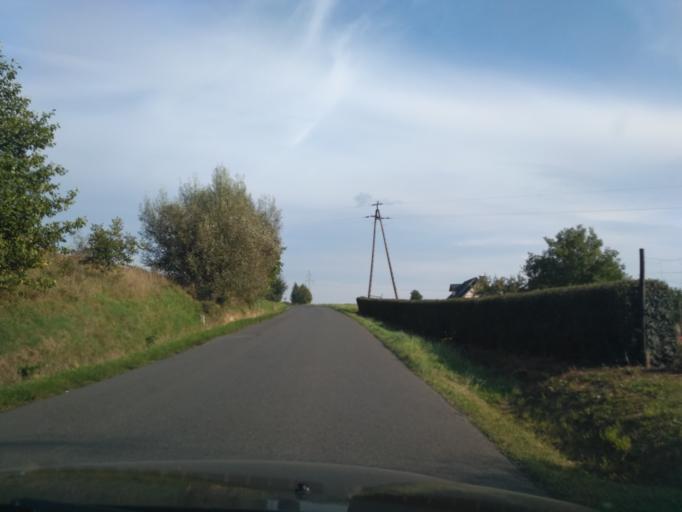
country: PL
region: Subcarpathian Voivodeship
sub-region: Powiat rzeszowski
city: Zglobien
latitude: 50.0077
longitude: 21.8603
